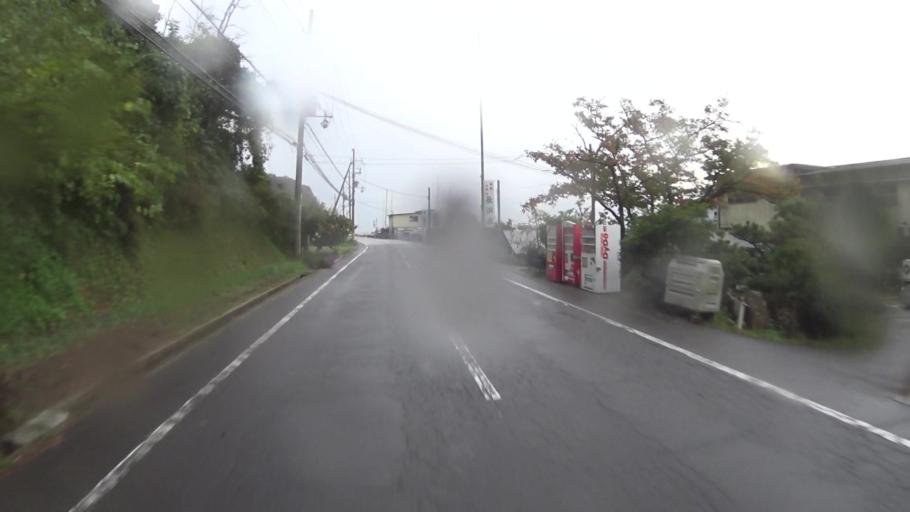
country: JP
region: Kyoto
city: Miyazu
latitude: 35.5602
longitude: 135.2049
